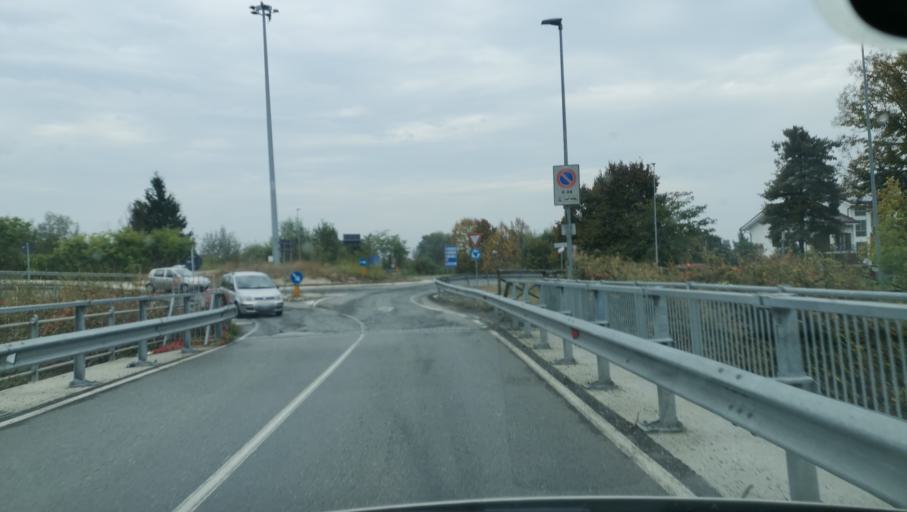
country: IT
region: Piedmont
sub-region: Provincia di Torino
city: Settimo Torinese
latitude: 45.1308
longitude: 7.7844
